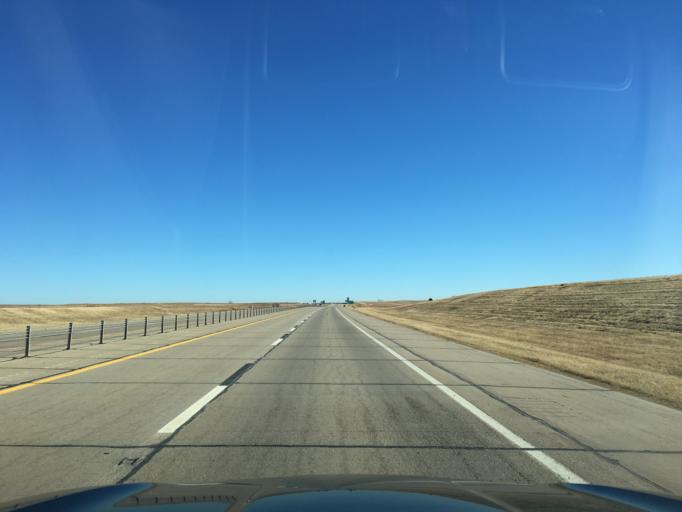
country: US
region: Oklahoma
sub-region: Noble County
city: Perry
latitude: 36.4000
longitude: -97.3149
